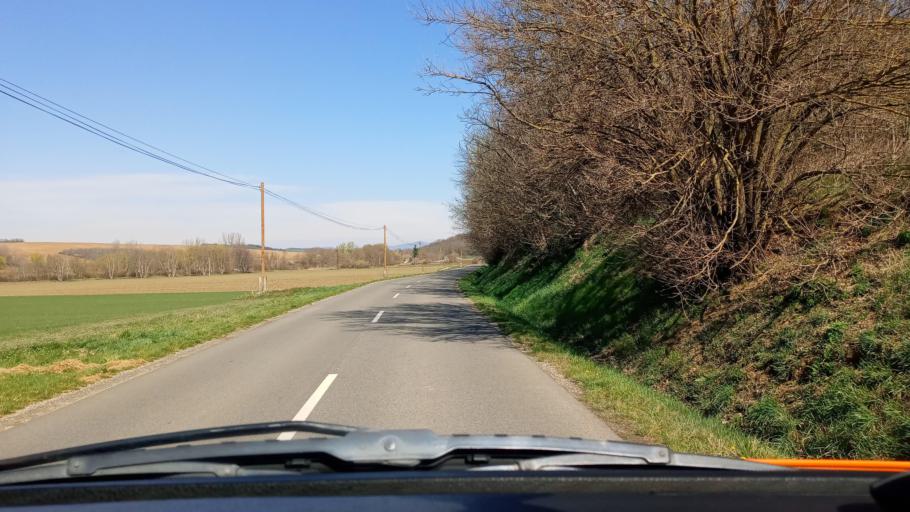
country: HU
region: Baranya
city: Boly
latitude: 46.0024
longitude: 18.4587
